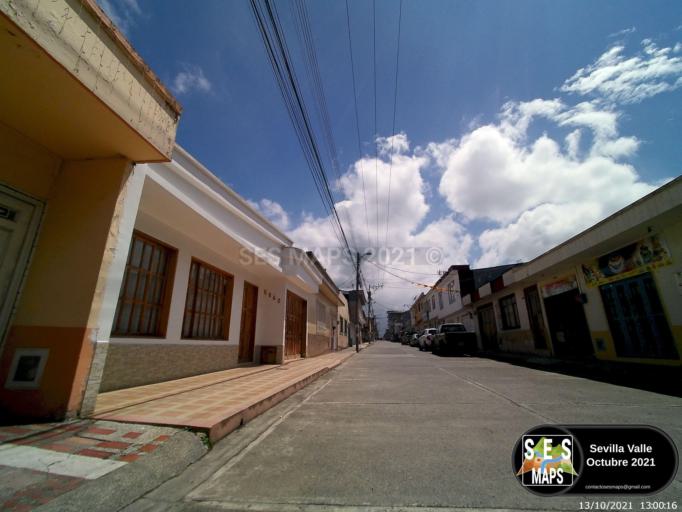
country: CO
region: Valle del Cauca
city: Sevilla
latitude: 4.2671
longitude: -75.9338
